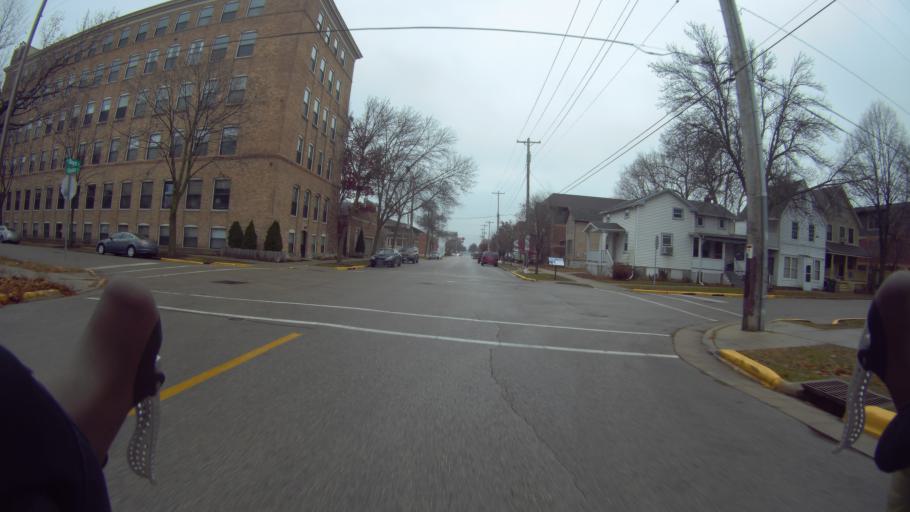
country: US
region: Wisconsin
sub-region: Dane County
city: Madison
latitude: 43.0814
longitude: -89.3791
